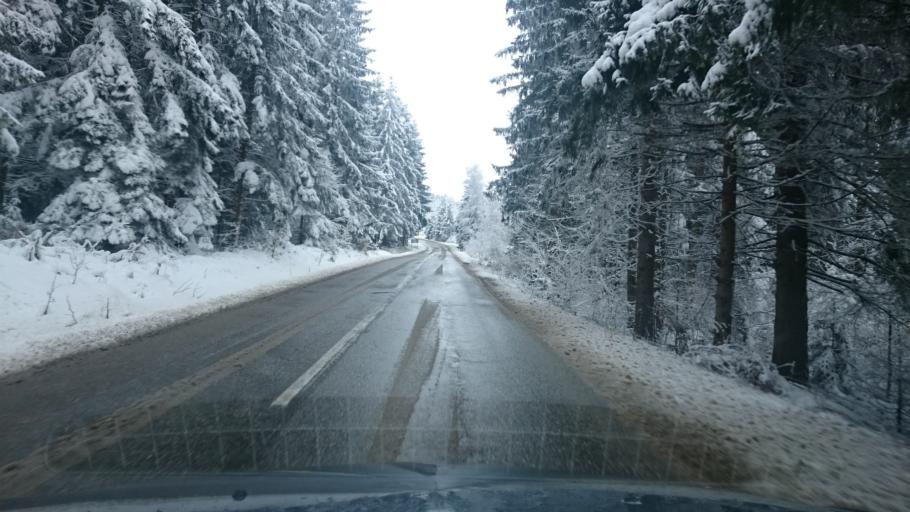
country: BA
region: Republika Srpska
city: Skender Vakuf
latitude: 44.5000
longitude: 17.3412
